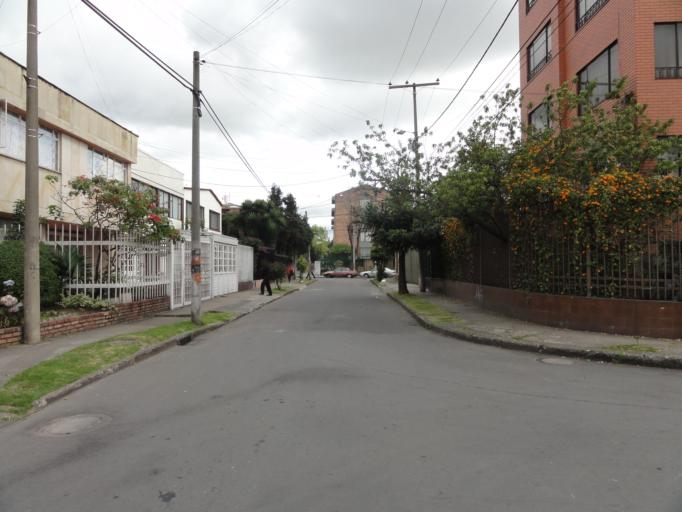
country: CO
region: Bogota D.C.
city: Bogota
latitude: 4.6480
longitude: -74.0802
